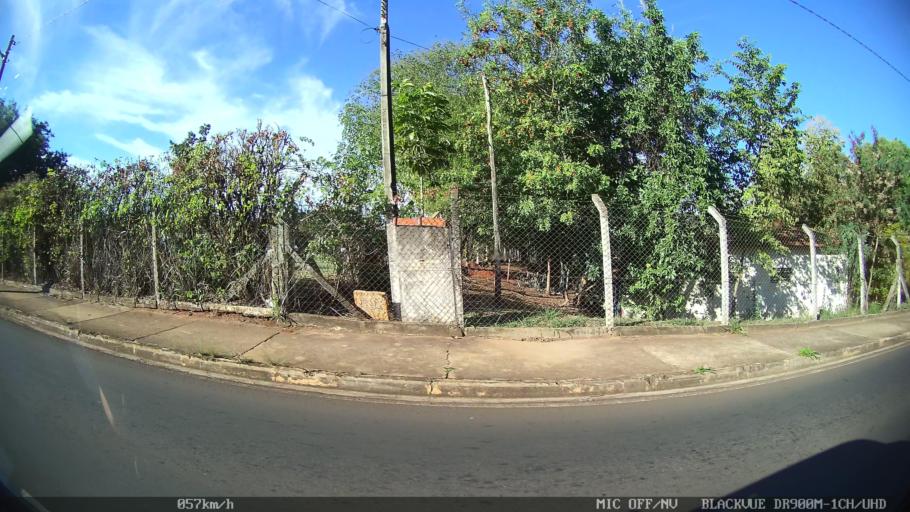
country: BR
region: Sao Paulo
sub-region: Araraquara
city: Araraquara
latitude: -21.7507
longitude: -48.1828
